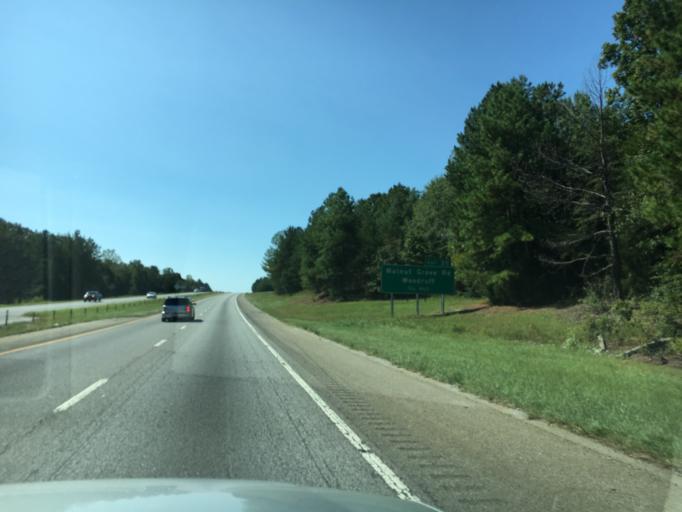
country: US
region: South Carolina
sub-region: Spartanburg County
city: Woodruff
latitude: 34.7631
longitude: -81.9541
